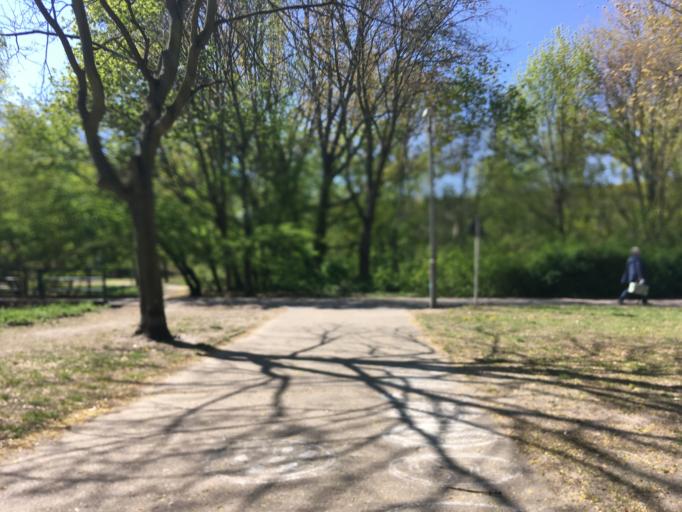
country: DE
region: Berlin
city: Friedrichsfelde
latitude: 52.5011
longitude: 13.5047
